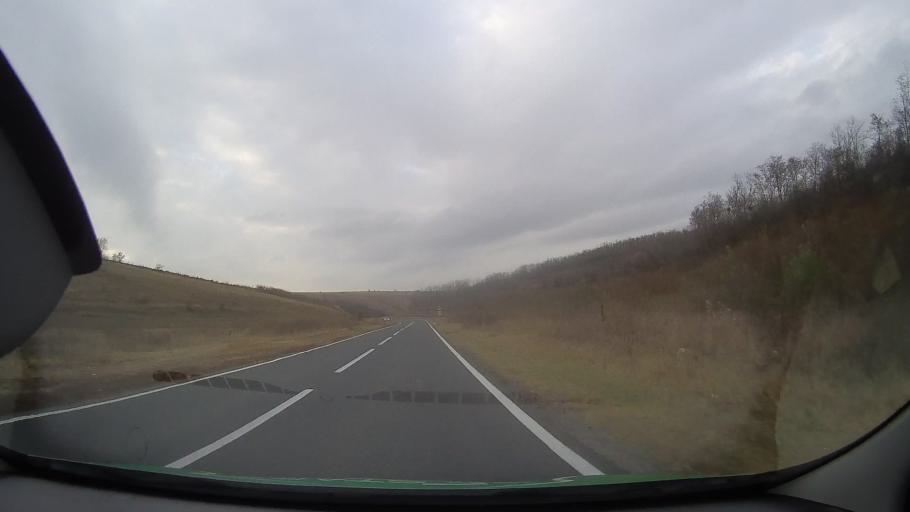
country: RO
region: Constanta
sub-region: Comuna Deleni
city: Deleni
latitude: 44.1013
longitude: 28.0279
